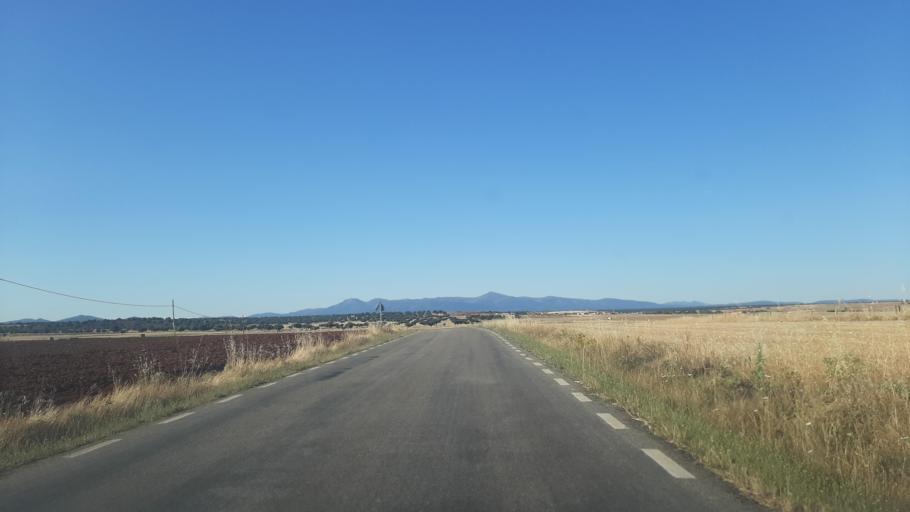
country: ES
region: Castille and Leon
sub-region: Provincia de Salamanca
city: Cabrillas
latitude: 40.7249
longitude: -6.1760
